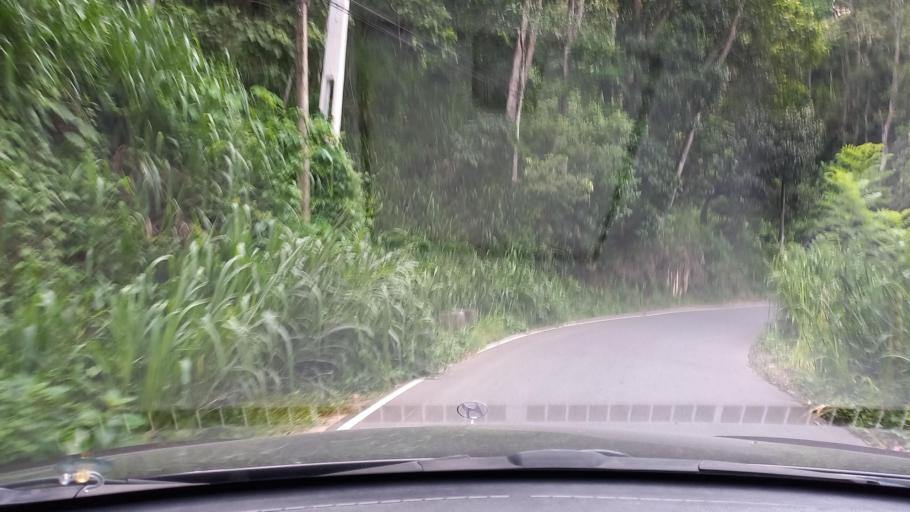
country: LK
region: Central
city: Gampola
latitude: 7.2259
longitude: 80.6065
